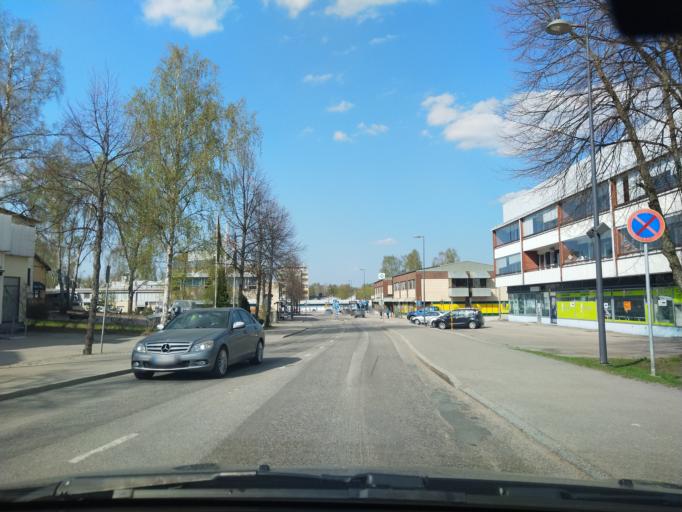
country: FI
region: Uusimaa
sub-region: Helsinki
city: Lohja
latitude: 60.1893
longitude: 23.9980
